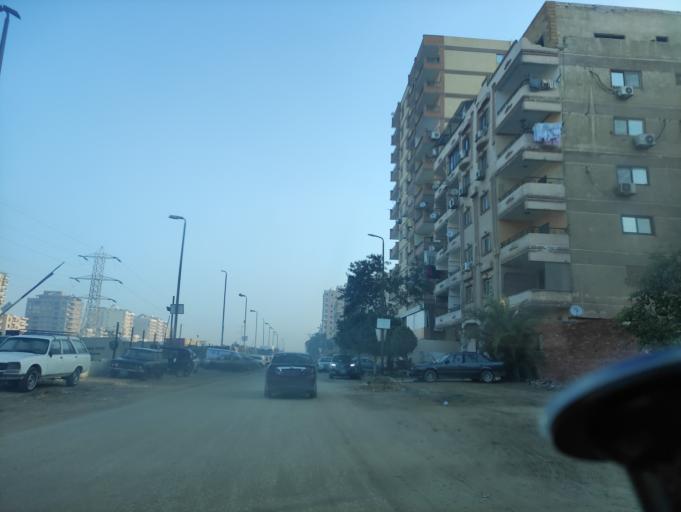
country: EG
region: Muhafazat al Qahirah
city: Cairo
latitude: 30.0501
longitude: 31.3690
